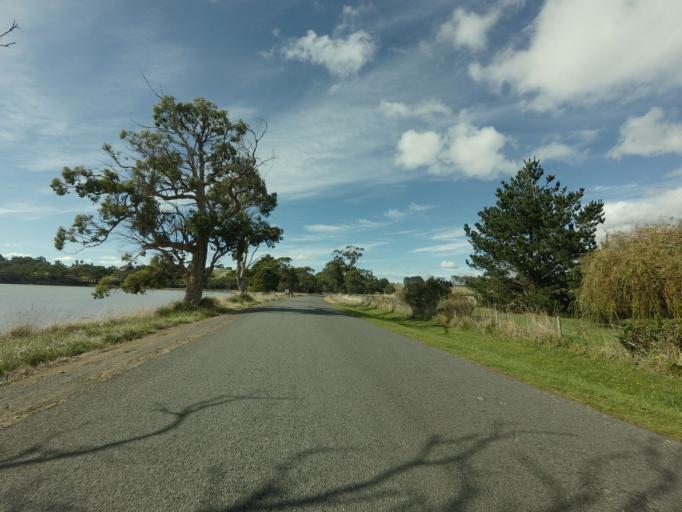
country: AU
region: Tasmania
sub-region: Clarence
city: Sandford
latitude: -43.0447
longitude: 147.7554
